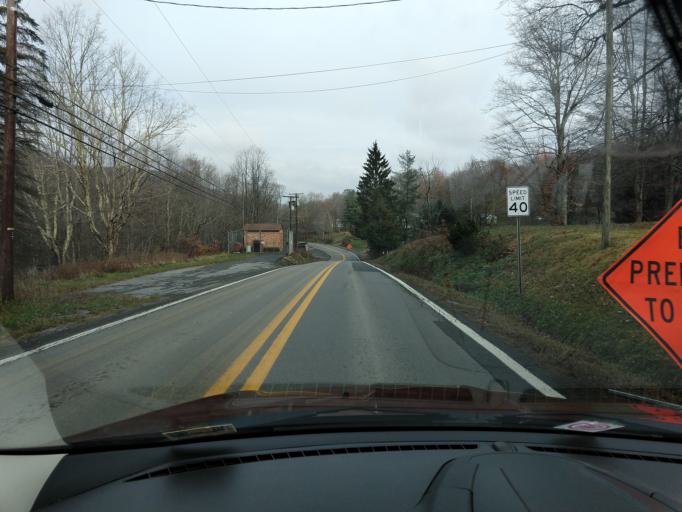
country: US
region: West Virginia
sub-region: Greenbrier County
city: Rainelle
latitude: 38.0609
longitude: -80.7081
